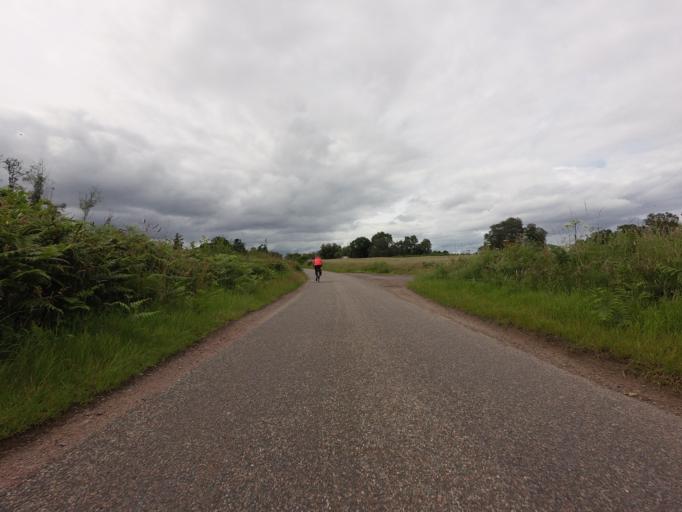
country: GB
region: Scotland
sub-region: Moray
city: Forres
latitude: 57.6047
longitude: -3.7491
